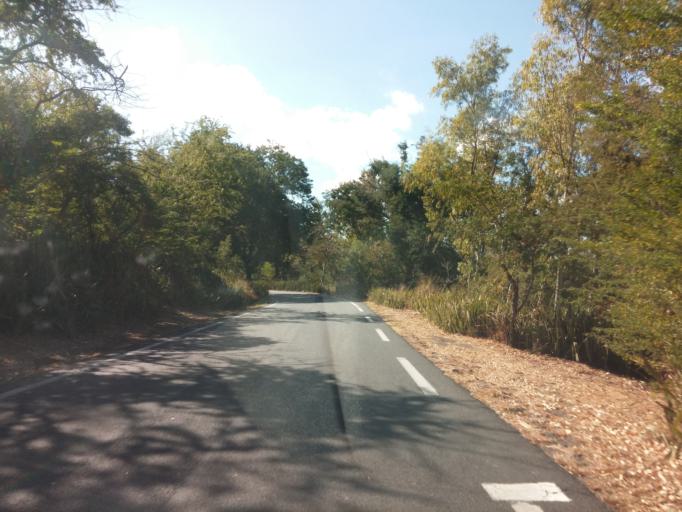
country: RE
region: Reunion
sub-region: Reunion
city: Les Avirons
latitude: -21.2614
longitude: 55.3485
